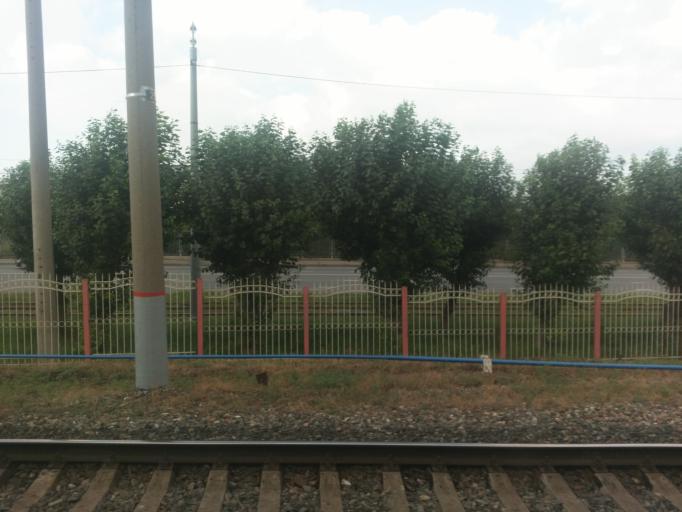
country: RU
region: Tatarstan
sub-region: Gorod Kazan'
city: Kazan
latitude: 55.7946
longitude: 49.0942
